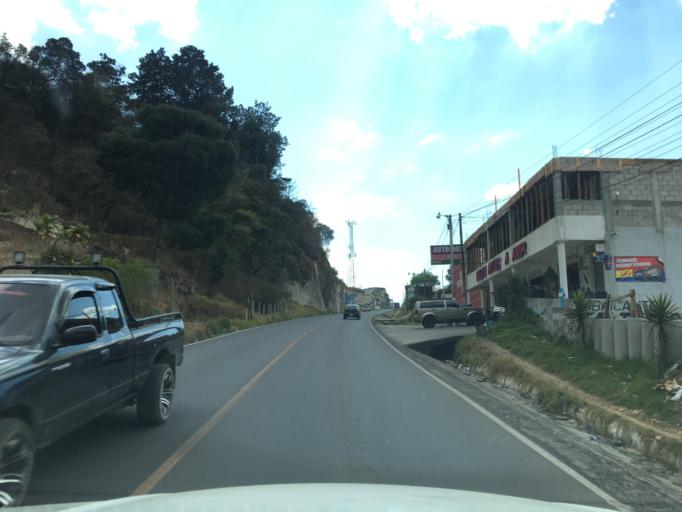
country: GT
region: Quetzaltenango
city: Olintepeque
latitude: 14.8813
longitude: -91.5144
